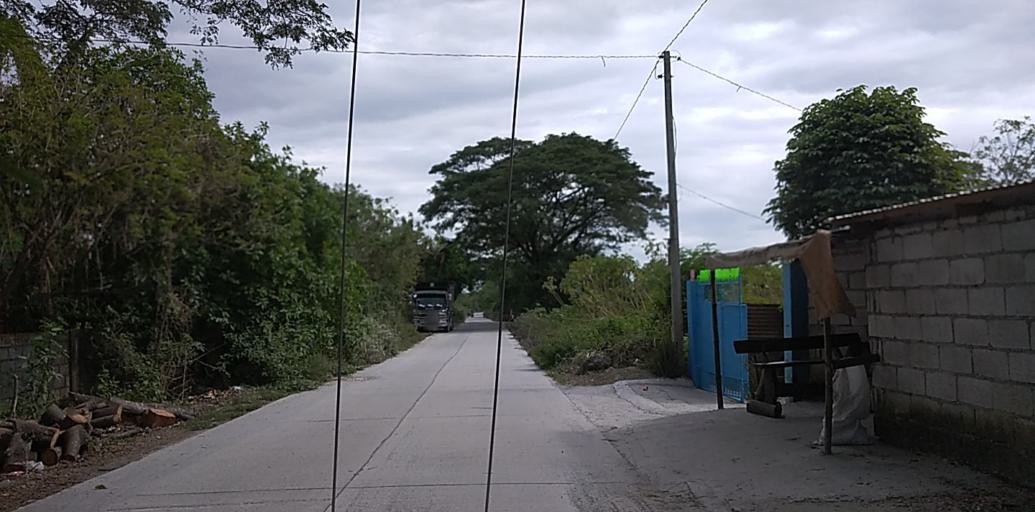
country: PH
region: Central Luzon
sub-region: Province of Pampanga
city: Pulung Santol
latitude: 15.0589
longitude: 120.5552
